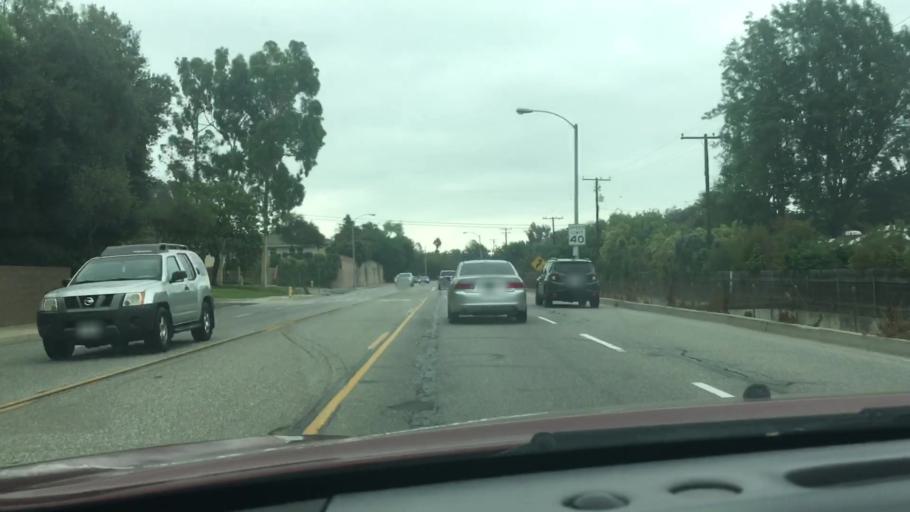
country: US
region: California
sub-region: Orange County
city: Fullerton
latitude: 33.8749
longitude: -117.9407
